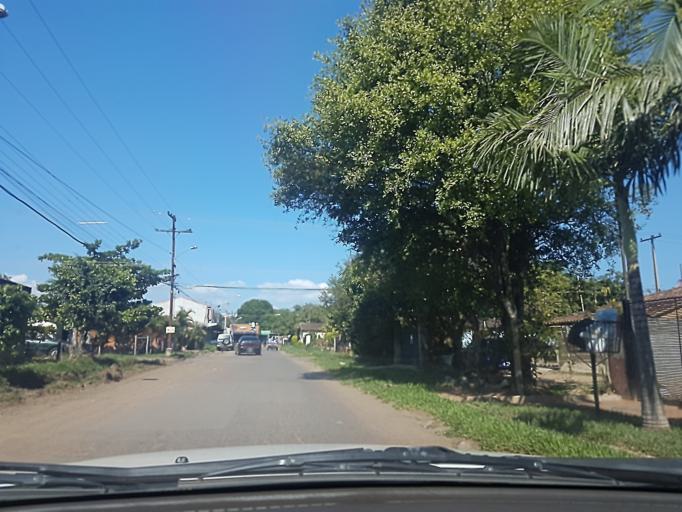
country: PY
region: Central
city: Limpio
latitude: -25.1738
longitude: -57.4737
